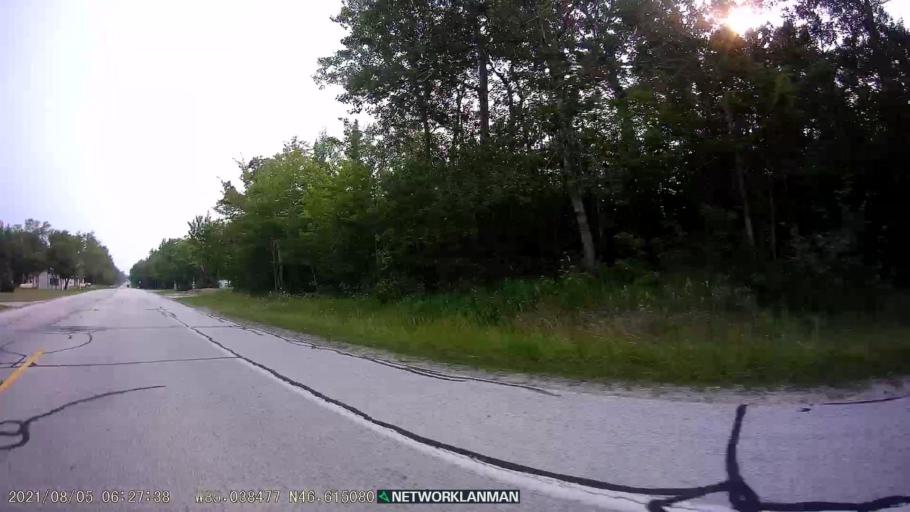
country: US
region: Michigan
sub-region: Luce County
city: Newberry
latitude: 46.6141
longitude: -85.0371
